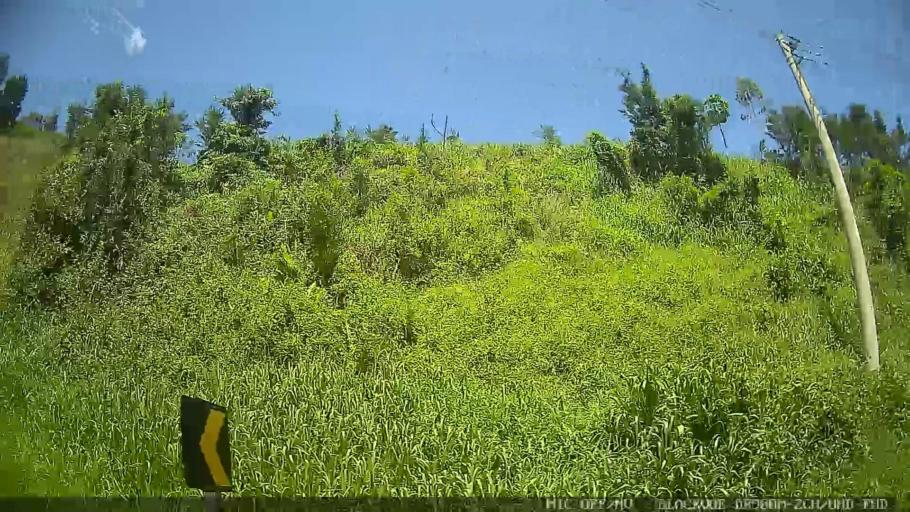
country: BR
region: Sao Paulo
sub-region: Caraguatatuba
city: Caraguatatuba
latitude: -23.5259
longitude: -45.5497
